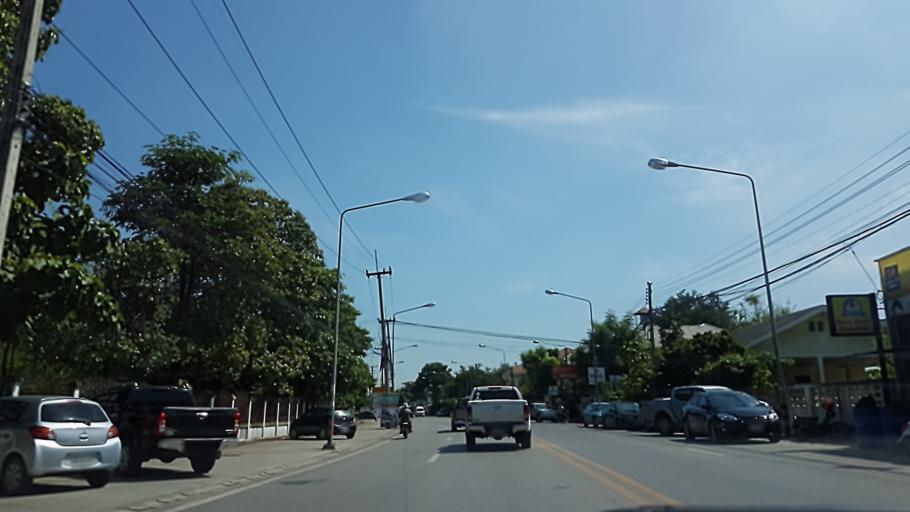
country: TH
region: Chiang Mai
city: Chiang Mai
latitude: 18.8192
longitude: 98.9738
